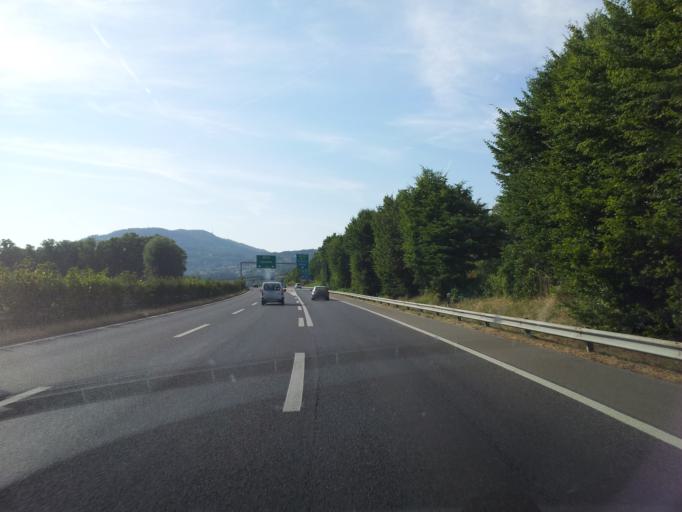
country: CH
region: Vaud
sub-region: Riviera-Pays-d'Enhaut District
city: La Tour-de-Peilz
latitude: 46.4663
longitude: 6.8742
